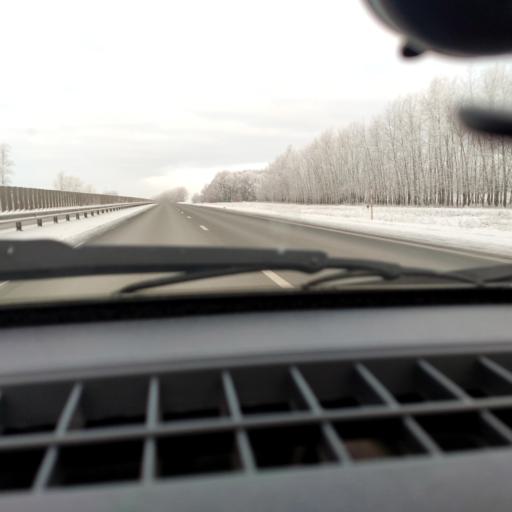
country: RU
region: Bashkortostan
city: Kushnarenkovo
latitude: 55.0443
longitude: 55.4482
